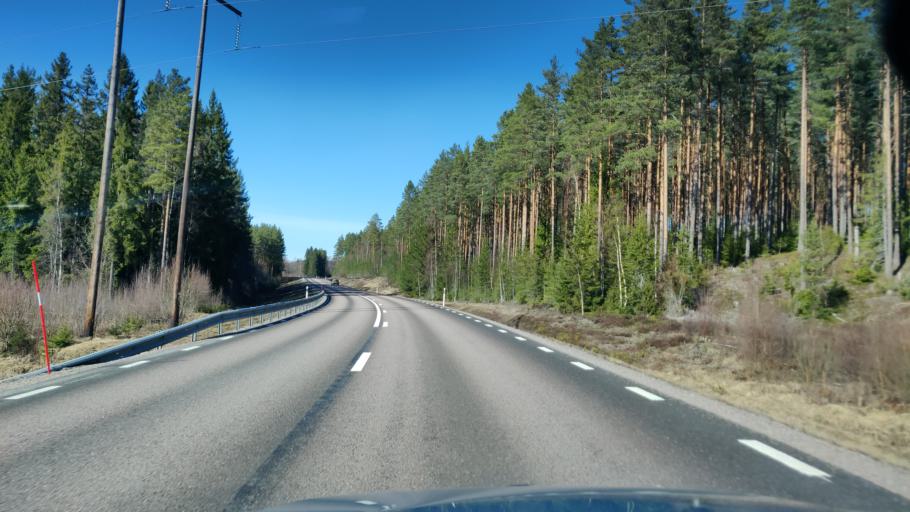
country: SE
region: Vaermland
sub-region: Hagfors Kommun
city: Hagfors
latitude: 59.9246
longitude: 13.6751
